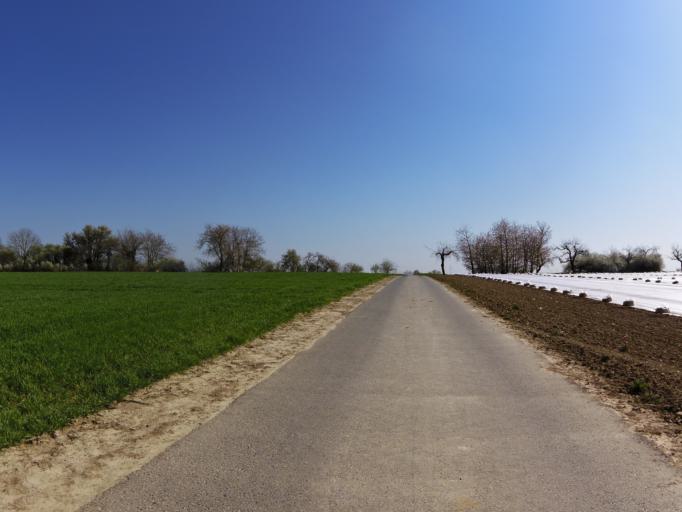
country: DE
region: Bavaria
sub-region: Regierungsbezirk Unterfranken
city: Oberpleichfeld
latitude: 49.8218
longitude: 10.0905
